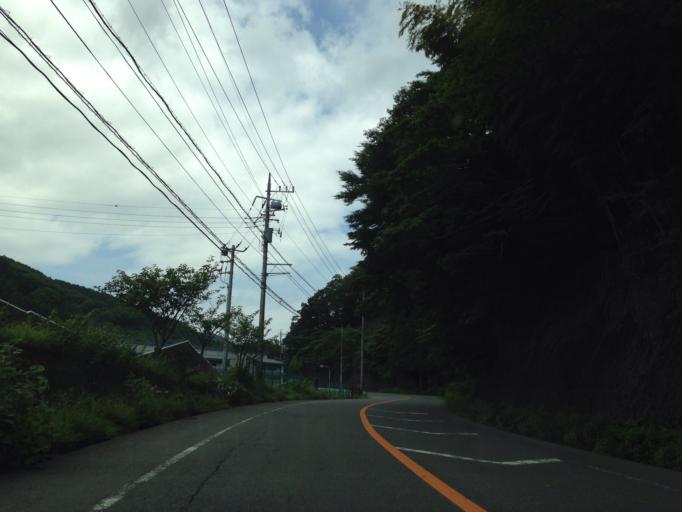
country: JP
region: Shizuoka
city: Heda
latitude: 34.9190
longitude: 138.8727
